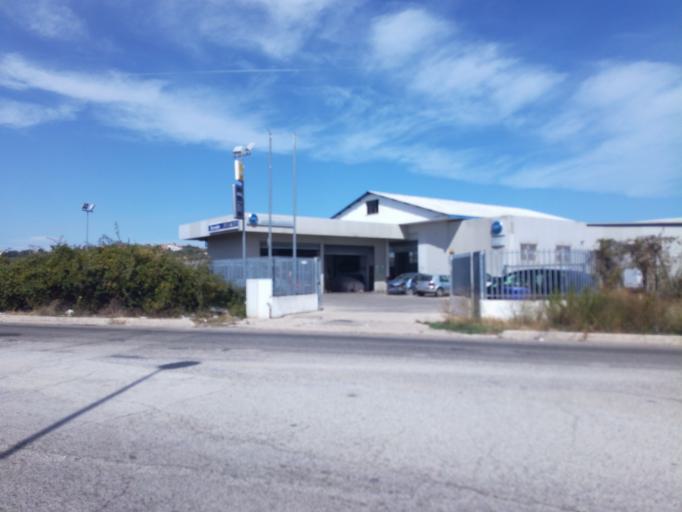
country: IT
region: Abruzzo
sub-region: Provincia di Chieti
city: Francavilla al Mare
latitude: 42.3981
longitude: 14.2928
